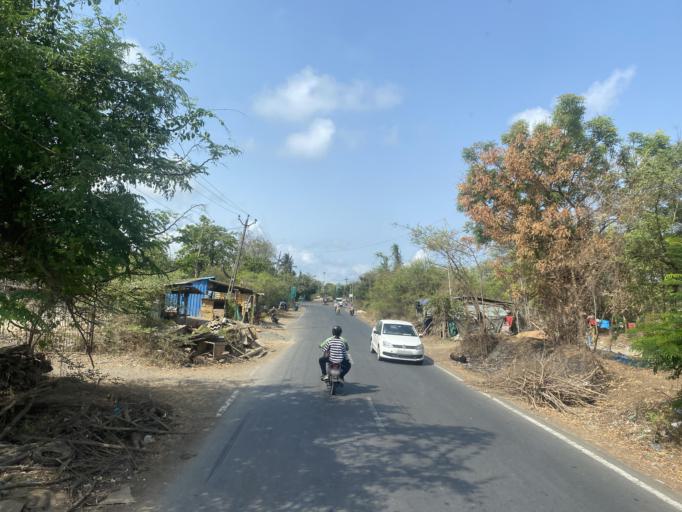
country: IN
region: Daman and Diu
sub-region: Daman District
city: Daman
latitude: 20.3378
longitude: 72.8028
